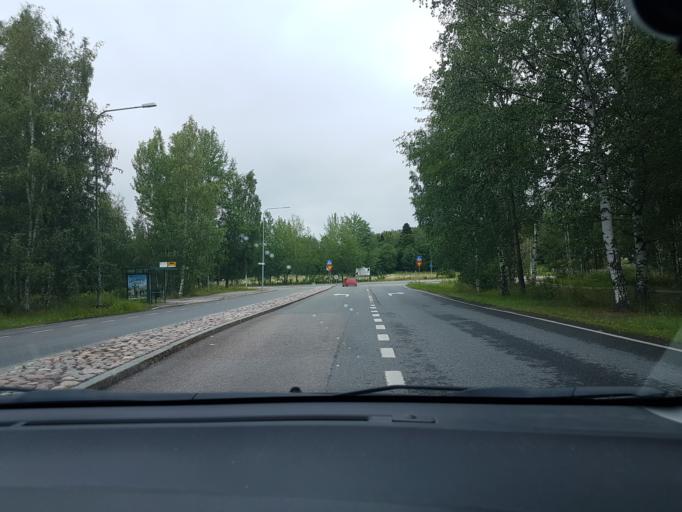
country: FI
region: Uusimaa
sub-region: Helsinki
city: Vantaa
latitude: 60.2648
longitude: 25.0422
